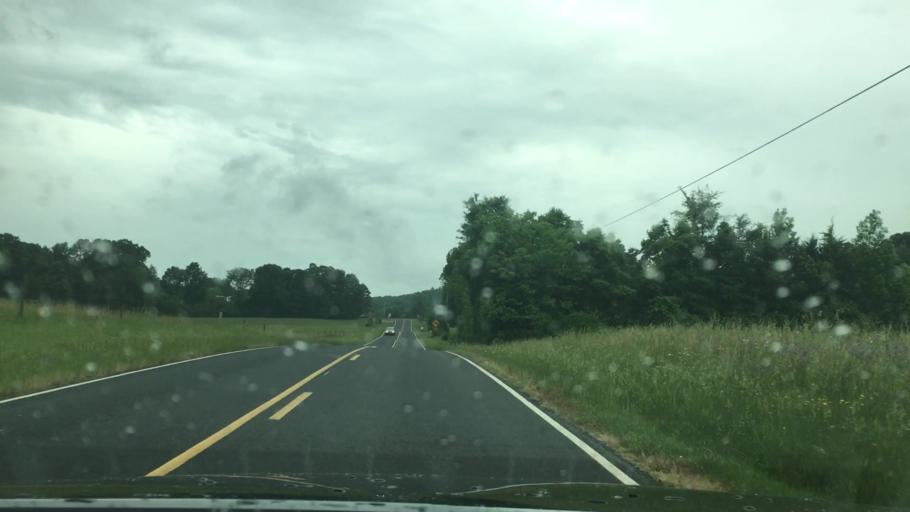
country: US
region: North Carolina
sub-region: Stanly County
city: Badin
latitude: 35.3771
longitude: -80.1159
